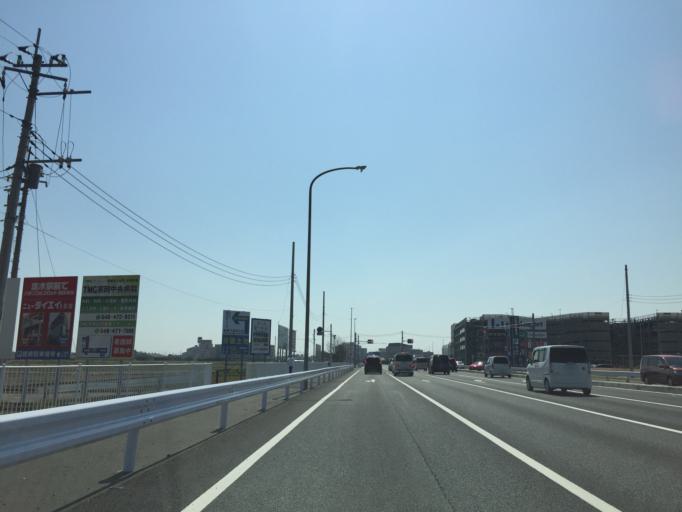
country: JP
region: Saitama
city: Oi
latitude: 35.8642
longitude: 139.5469
